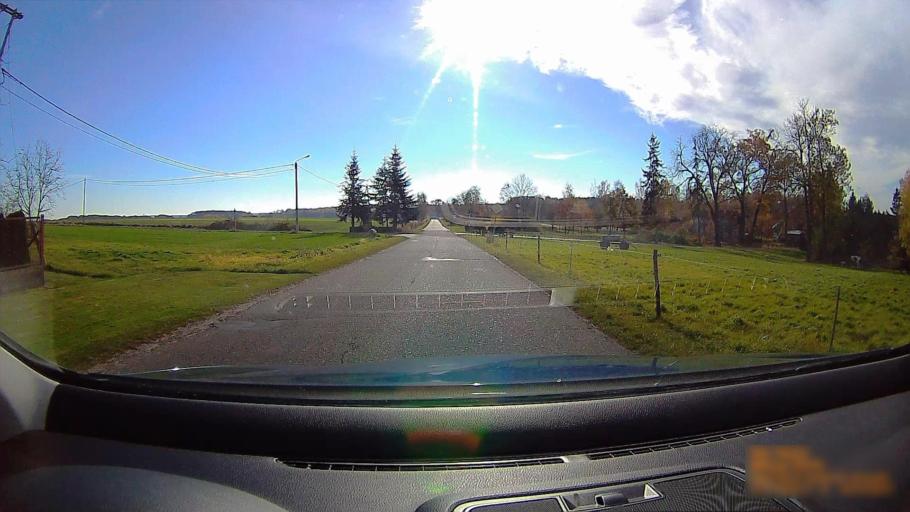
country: PL
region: Greater Poland Voivodeship
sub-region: Powiat ostrzeszowski
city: Doruchow
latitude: 51.3957
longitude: 18.0306
